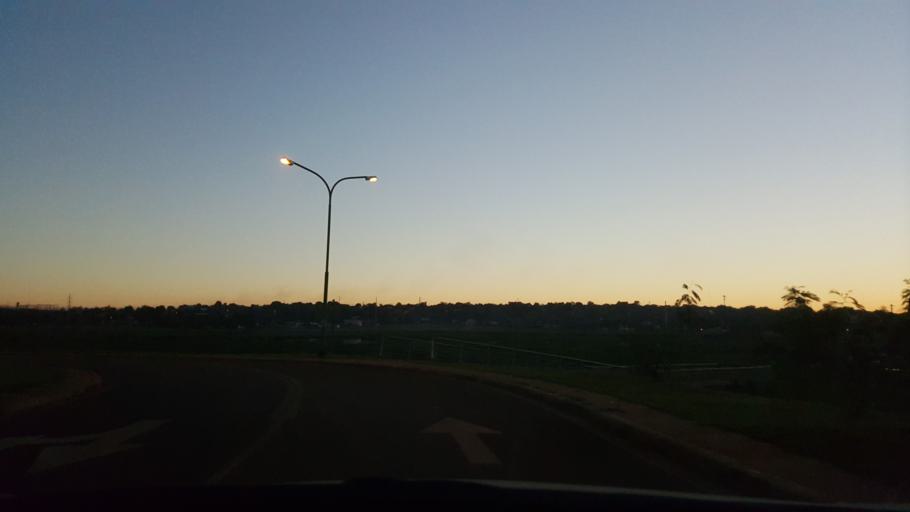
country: AR
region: Misiones
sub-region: Departamento de Capital
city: Posadas
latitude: -27.4220
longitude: -55.9045
